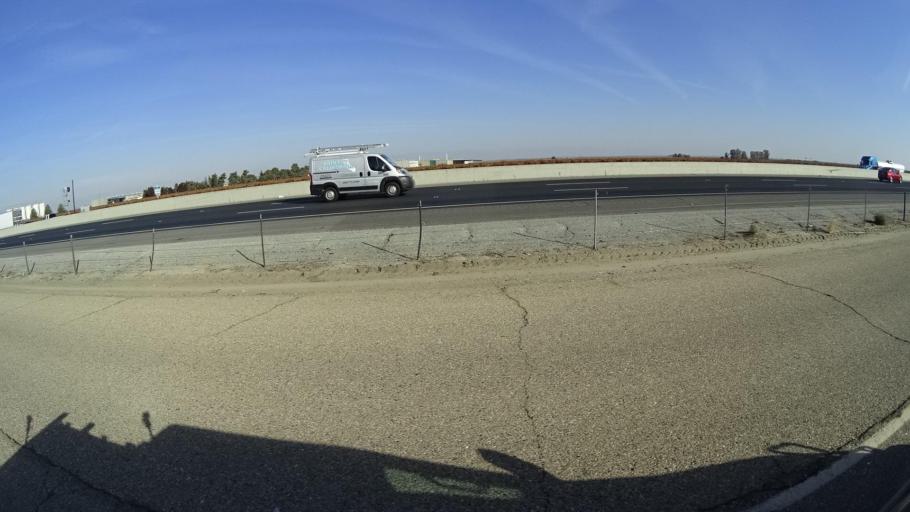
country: US
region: California
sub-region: Kern County
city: McFarland
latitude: 35.7002
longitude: -119.2332
